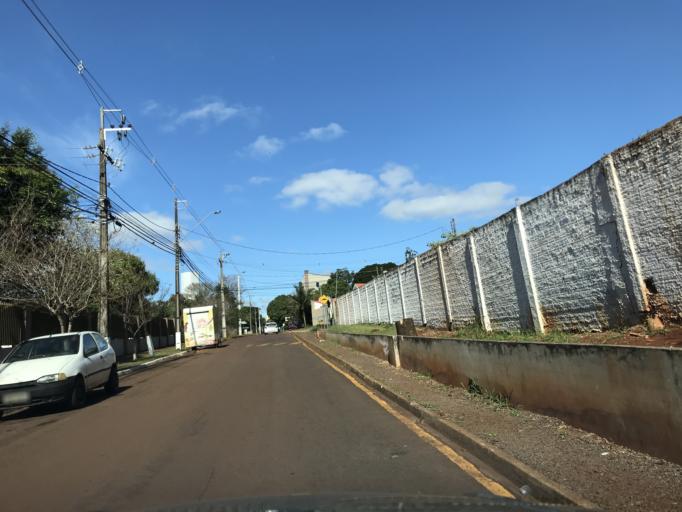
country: BR
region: Parana
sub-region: Cascavel
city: Cascavel
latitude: -24.9366
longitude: -53.4697
